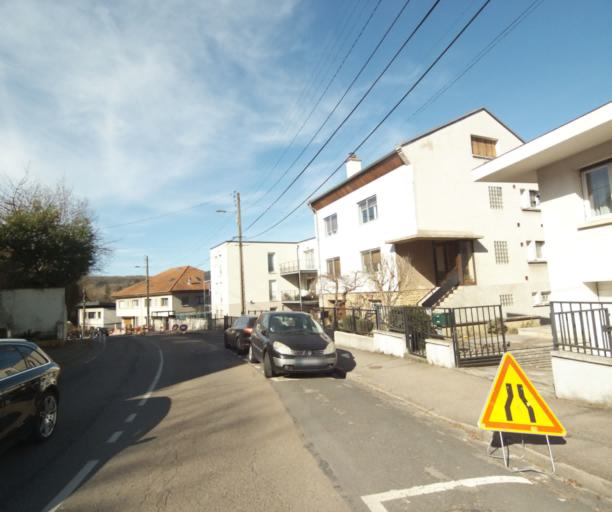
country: FR
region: Lorraine
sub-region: Departement de Meurthe-et-Moselle
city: Villers-les-Nancy
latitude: 48.6733
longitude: 6.1467
